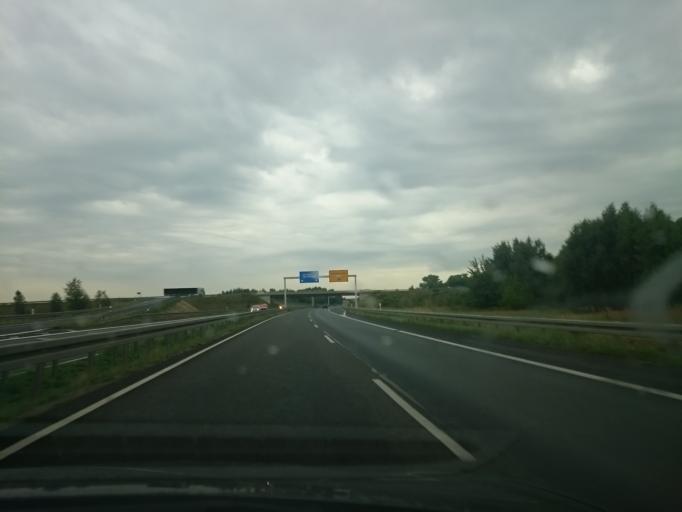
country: DE
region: Brandenburg
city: Leegebruch
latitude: 52.7222
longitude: 13.2177
